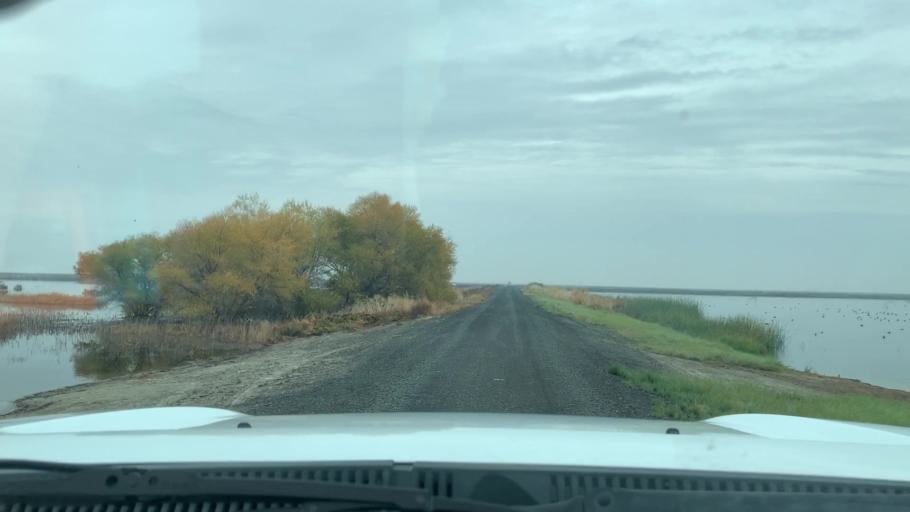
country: US
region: California
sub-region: Tulare County
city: Alpaugh
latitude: 35.7485
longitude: -119.5835
